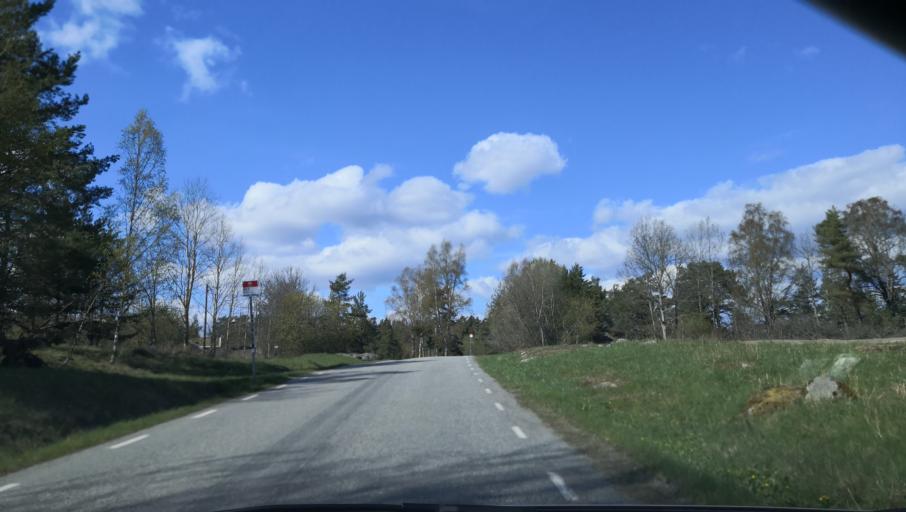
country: SE
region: Stockholm
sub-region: Varmdo Kommun
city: Hemmesta
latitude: 59.4060
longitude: 18.5051
